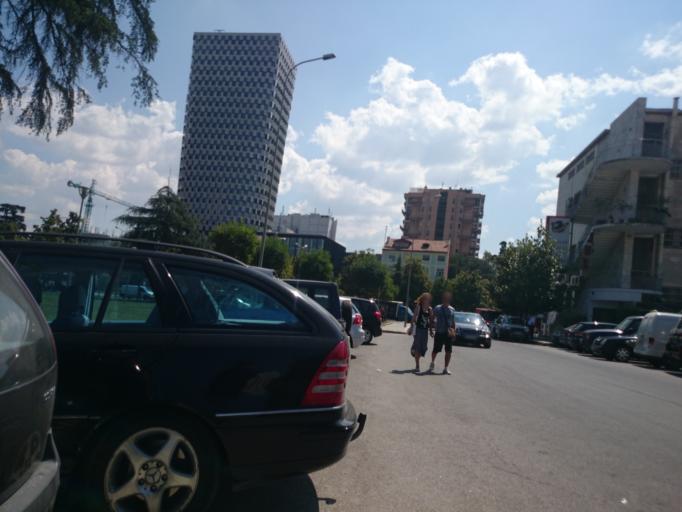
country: AL
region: Tirane
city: Tirana
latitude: 41.3291
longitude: 19.8203
